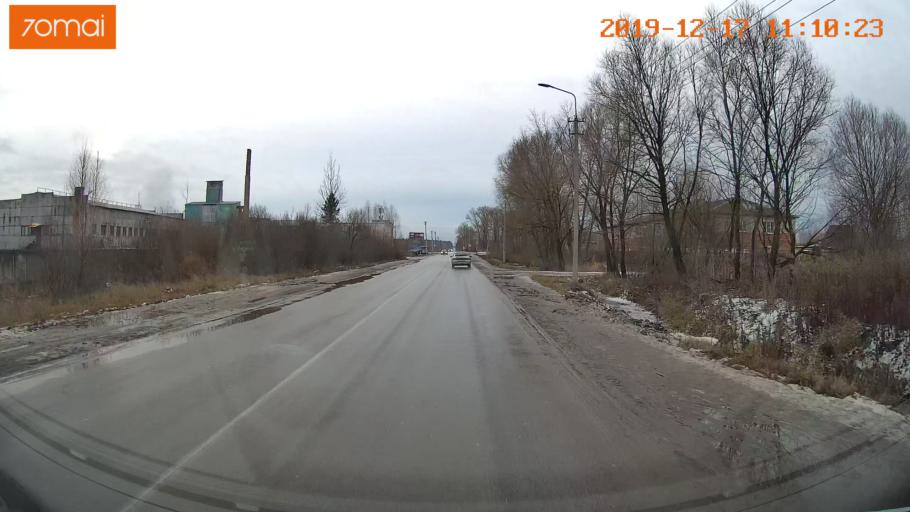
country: RU
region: Vladimir
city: Gus'-Khrustal'nyy
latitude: 55.5931
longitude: 40.6418
